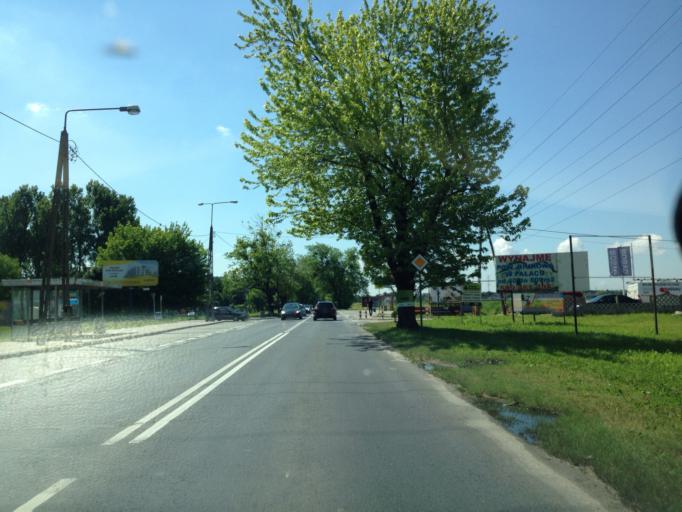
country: PL
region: Masovian Voivodeship
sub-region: Warszawa
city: Bemowo
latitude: 52.2323
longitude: 20.8968
